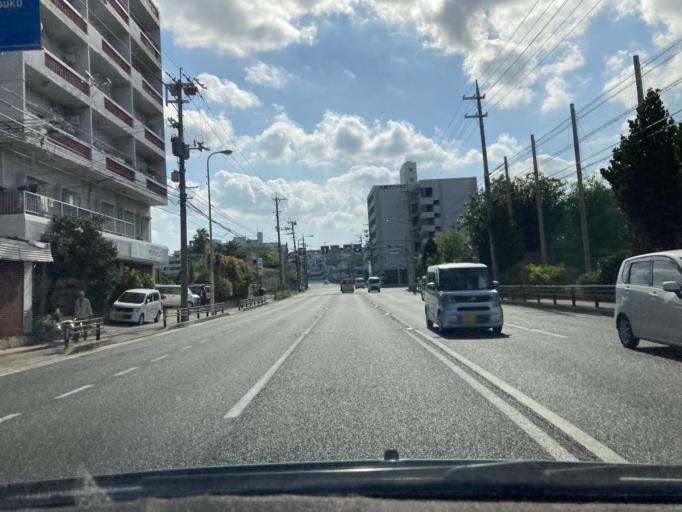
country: JP
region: Okinawa
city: Tomigusuku
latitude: 26.1976
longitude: 127.6895
